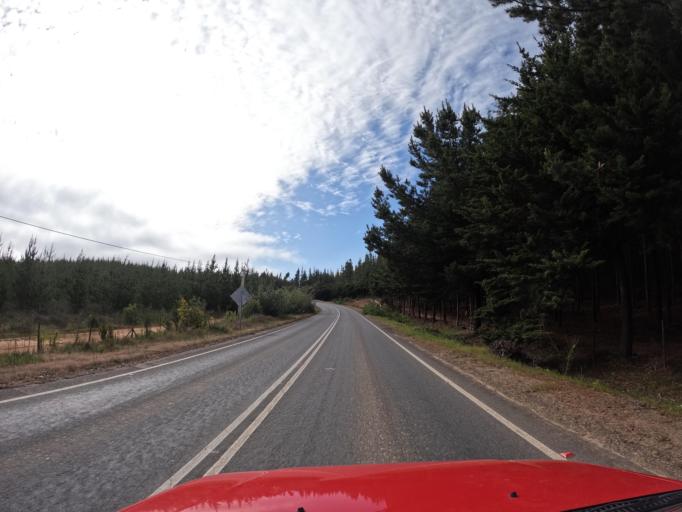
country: CL
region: O'Higgins
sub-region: Provincia de Colchagua
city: Santa Cruz
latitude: -34.3456
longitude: -71.8707
